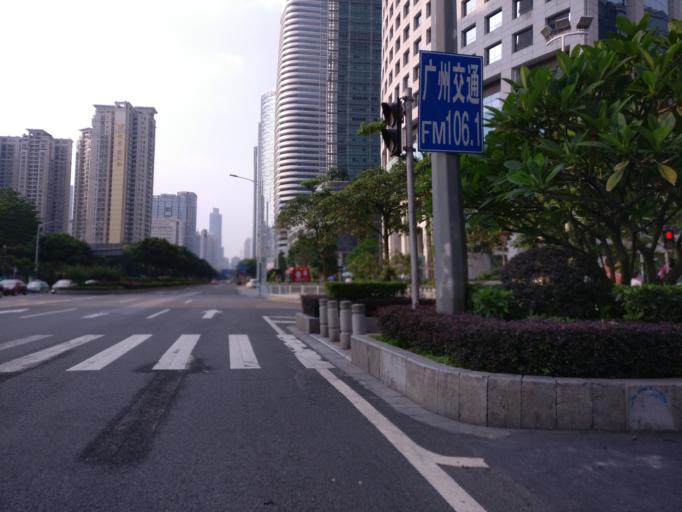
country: CN
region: Guangdong
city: Wushan
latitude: 23.1221
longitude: 113.3160
